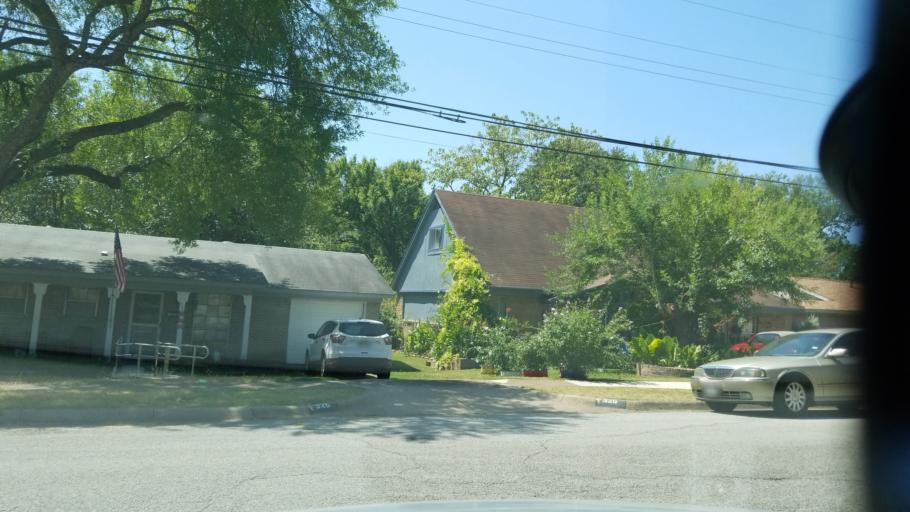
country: US
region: Texas
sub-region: Dallas County
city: Duncanville
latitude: 32.6526
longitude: -96.9044
